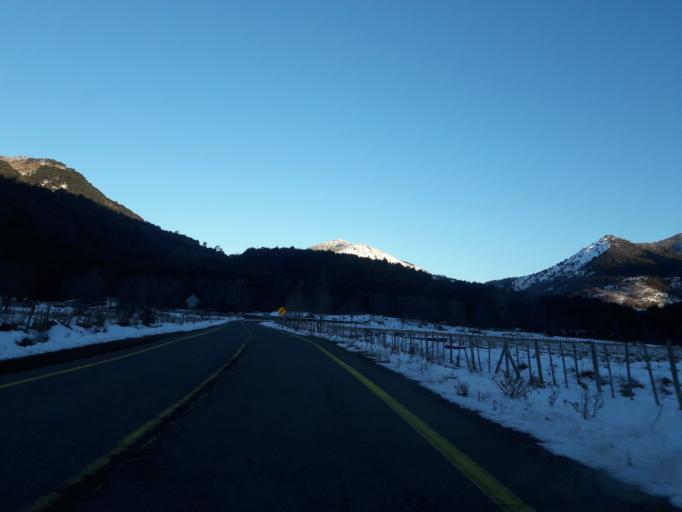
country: CL
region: Araucania
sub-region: Provincia de Cautin
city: Vilcun
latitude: -38.4984
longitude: -71.5210
